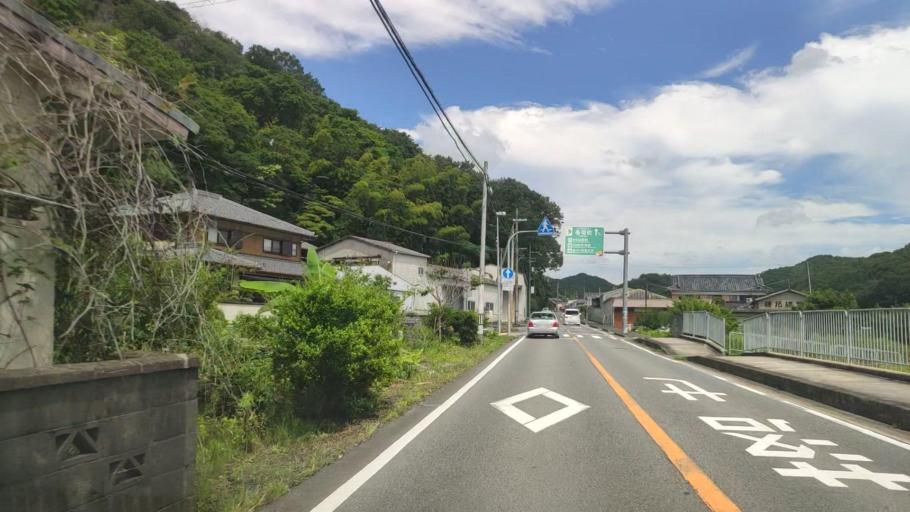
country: JP
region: Hyogo
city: Nishiwaki
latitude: 35.0169
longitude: 134.9532
